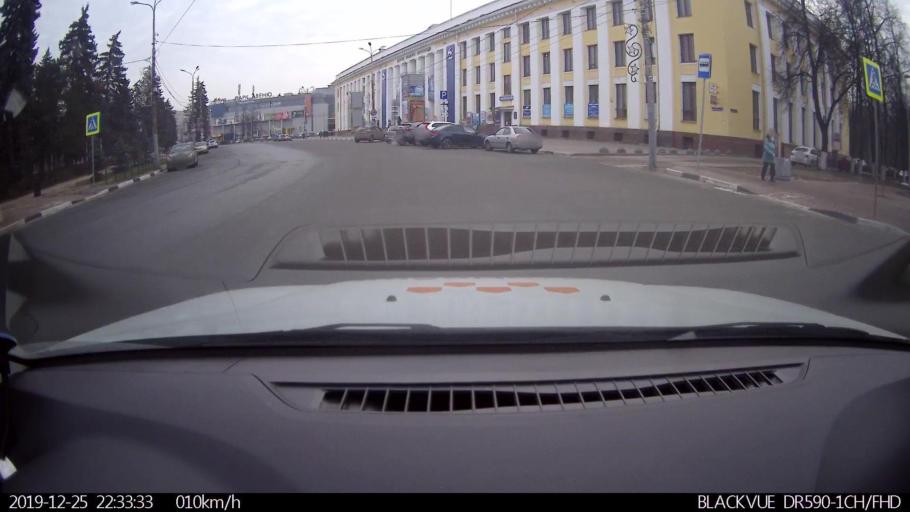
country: RU
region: Nizjnij Novgorod
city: Gorbatovka
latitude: 56.2408
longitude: 43.8608
